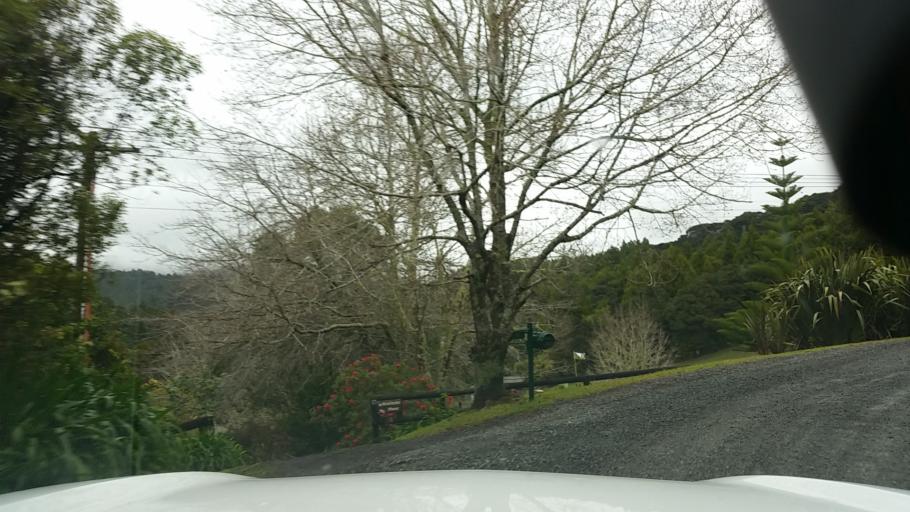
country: NZ
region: Auckland
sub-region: Auckland
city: Waitakere
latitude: -36.9020
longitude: 174.5705
